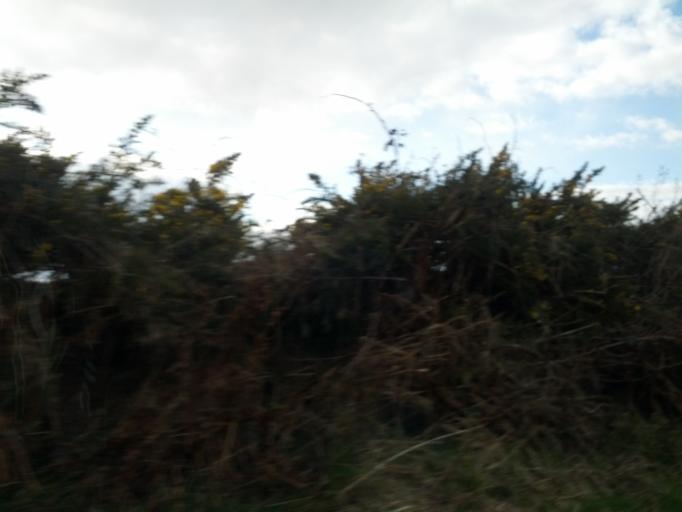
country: IE
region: Connaught
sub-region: County Galway
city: Athenry
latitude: 53.4610
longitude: -8.6466
